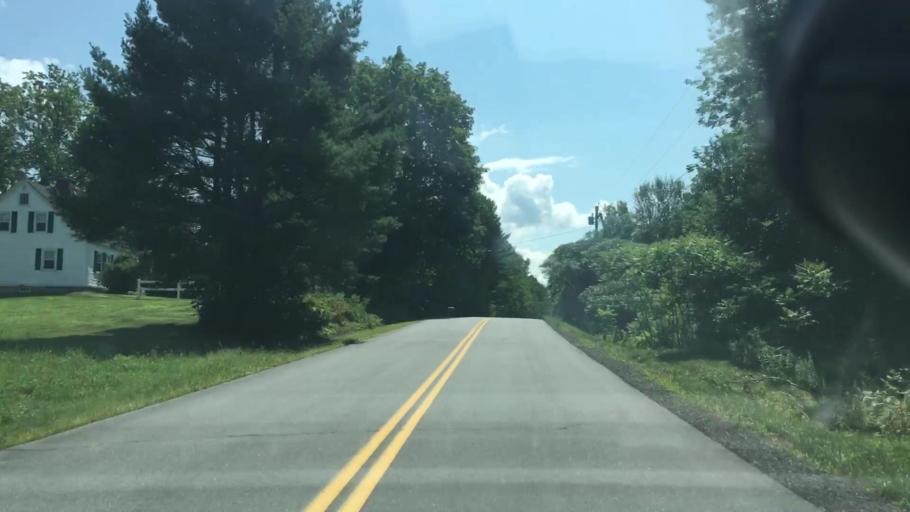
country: US
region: Maine
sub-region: Somerset County
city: Skowhegan
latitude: 44.6967
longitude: -69.6938
